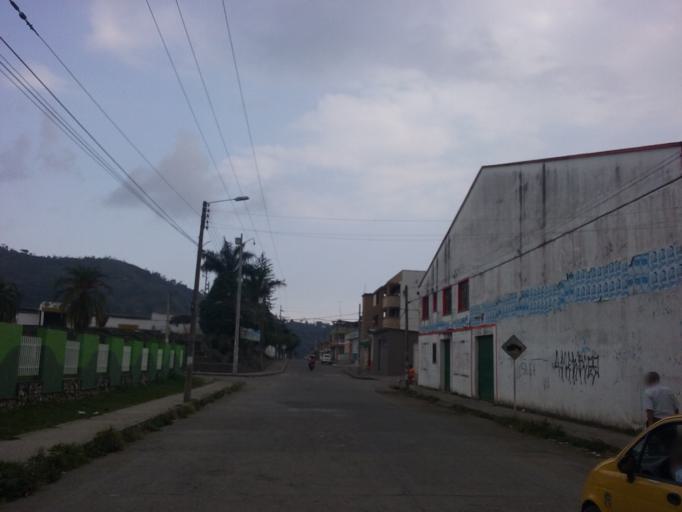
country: CO
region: Tolima
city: Libano
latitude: 4.9232
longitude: -75.0616
